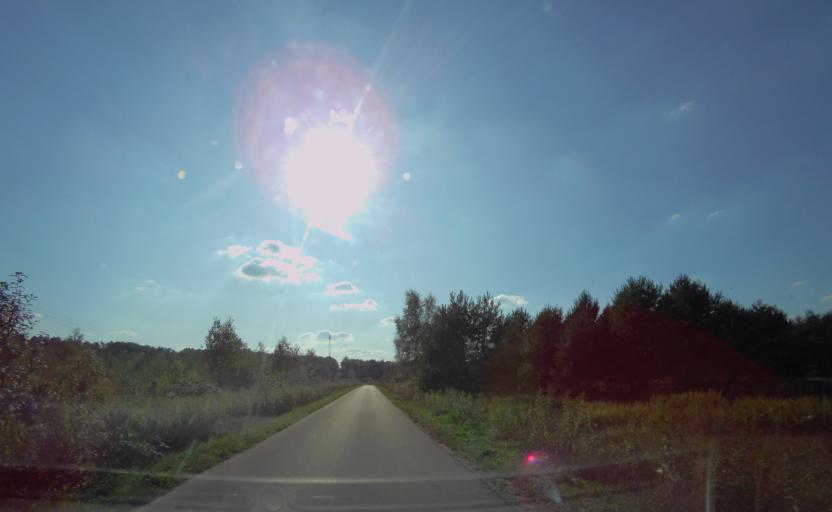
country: PL
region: Subcarpathian Voivodeship
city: Nowa Sarzyna
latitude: 50.2981
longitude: 22.3803
